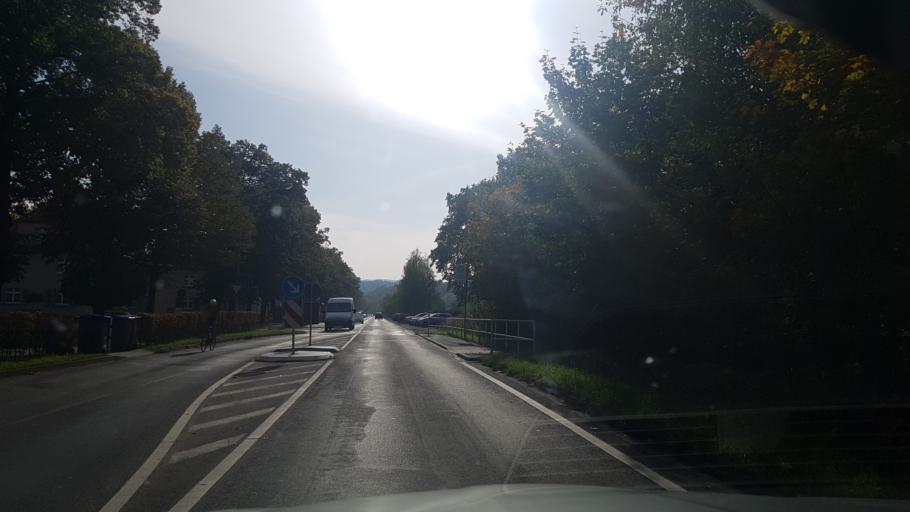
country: DE
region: Saxony
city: Pirna
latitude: 50.9378
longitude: 13.9453
